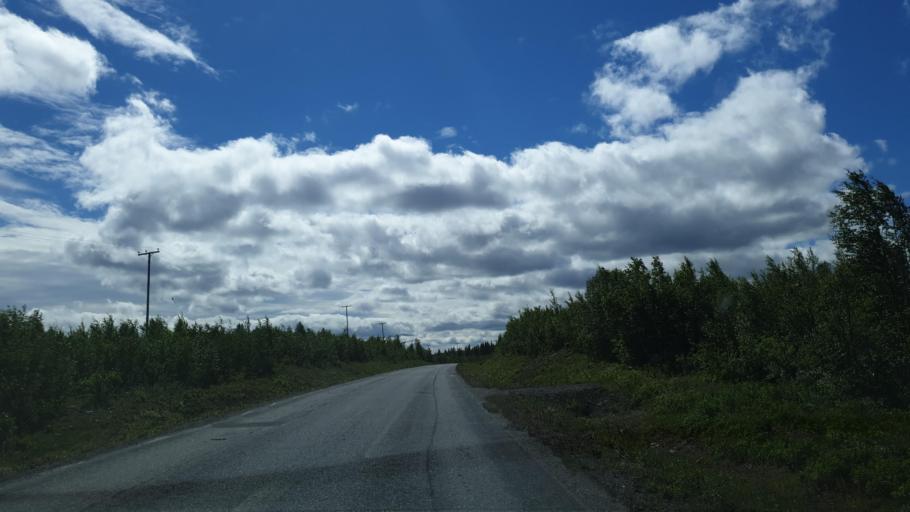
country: SE
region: Vaesterbotten
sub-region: Vilhelmina Kommun
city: Sjoberg
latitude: 65.0064
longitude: 15.8444
